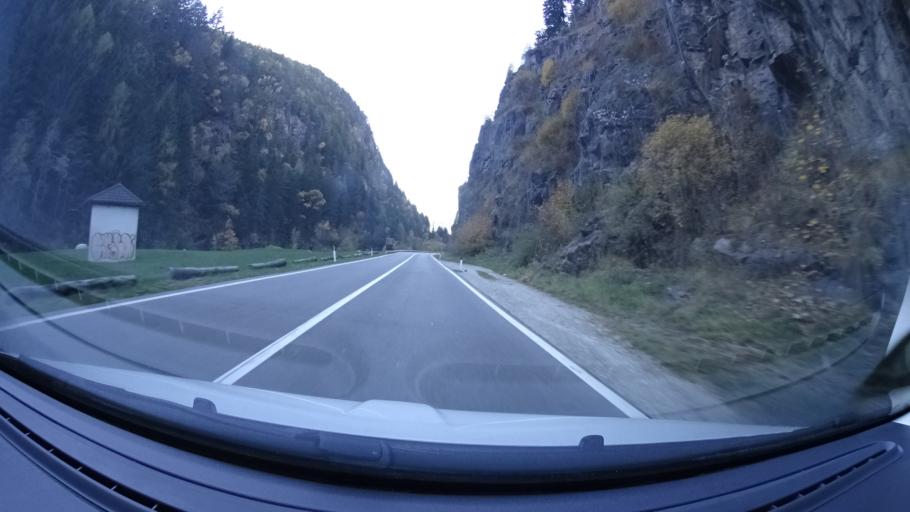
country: IT
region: Trentino-Alto Adige
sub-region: Bolzano
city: Ortisei
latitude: 46.5776
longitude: 11.6426
